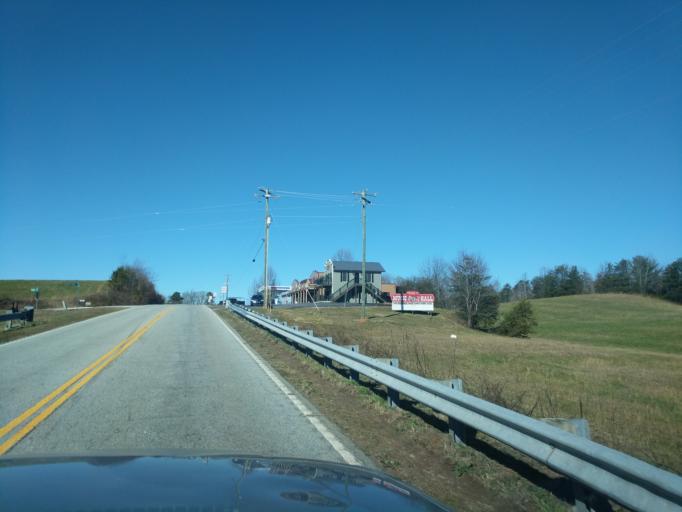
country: US
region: Georgia
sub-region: Rabun County
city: Clayton
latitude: 34.7680
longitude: -83.2548
